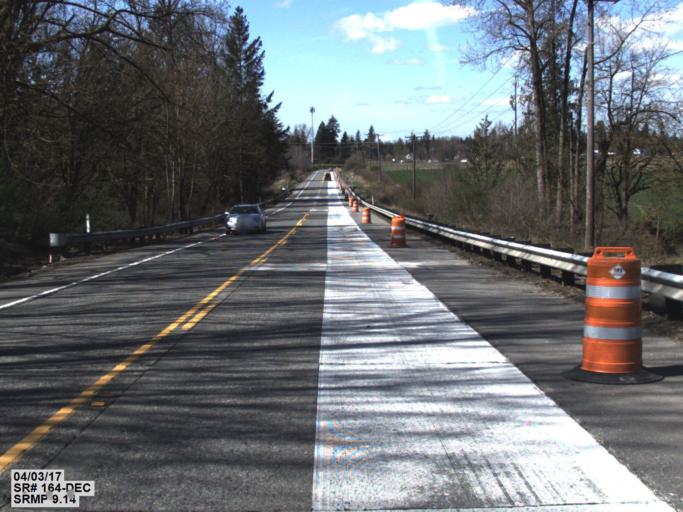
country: US
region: Washington
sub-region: Pierce County
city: Buckley
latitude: 47.2222
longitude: -122.0961
